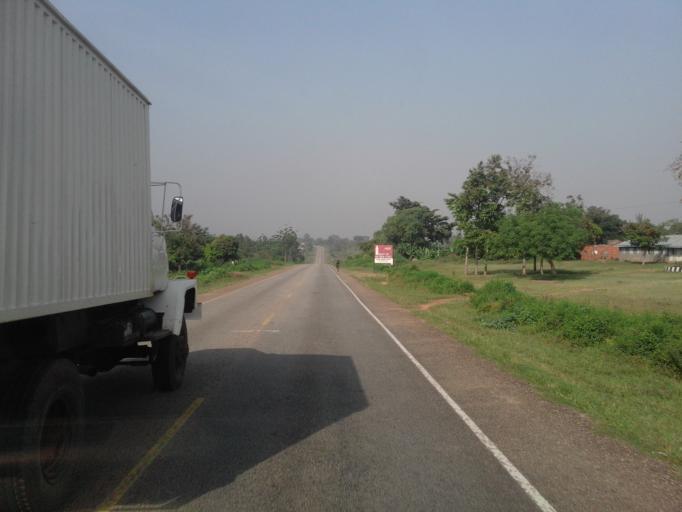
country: UG
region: Eastern Region
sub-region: Budaka District
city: Budaka
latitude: 1.0388
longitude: 34.0133
